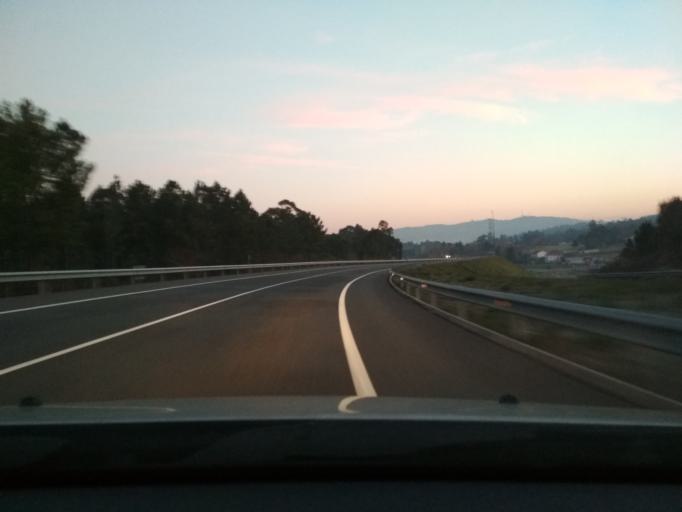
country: ES
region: Galicia
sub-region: Provincia da Coruna
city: Santiago de Compostela
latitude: 42.8430
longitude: -8.5947
